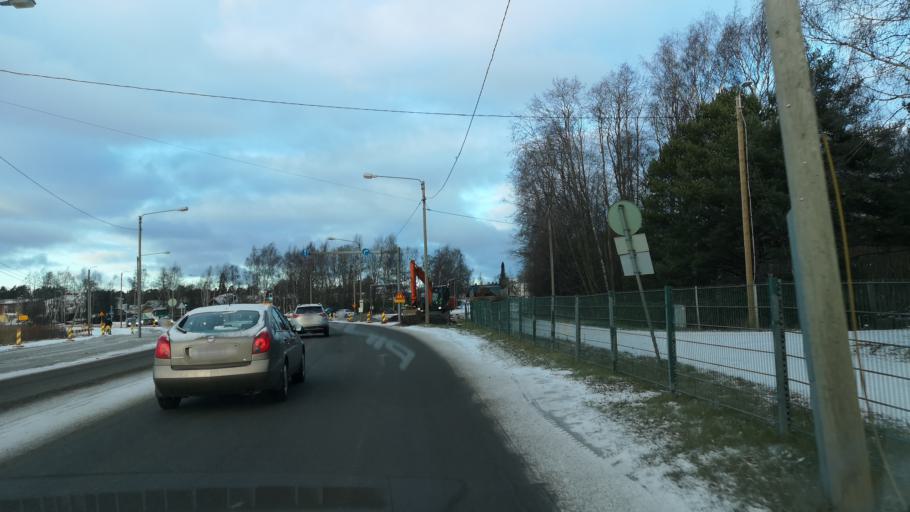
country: FI
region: Ostrobothnia
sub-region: Vaasa
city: Vaasa
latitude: 63.1125
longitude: 21.6187
